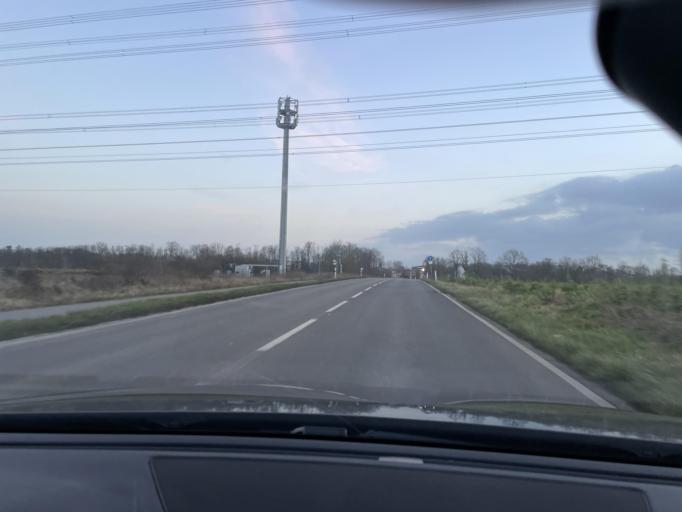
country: DE
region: North Rhine-Westphalia
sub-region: Regierungsbezirk Dusseldorf
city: Viersen
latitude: 51.2243
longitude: 6.4145
